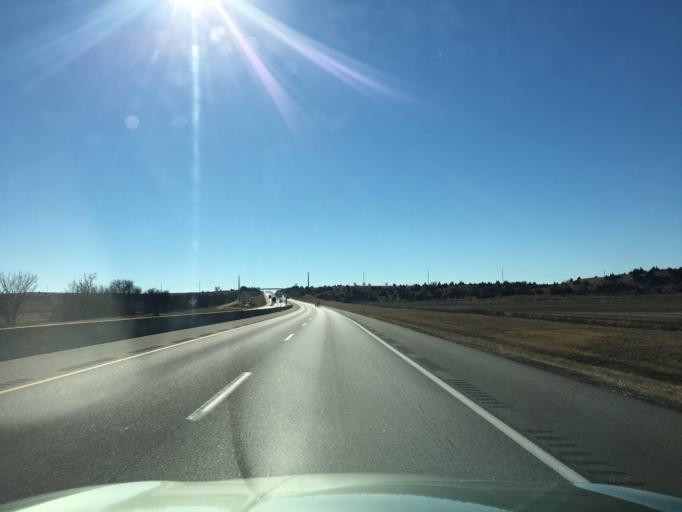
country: US
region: Kansas
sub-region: Sumner County
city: Wellington
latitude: 37.2143
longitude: -97.3397
